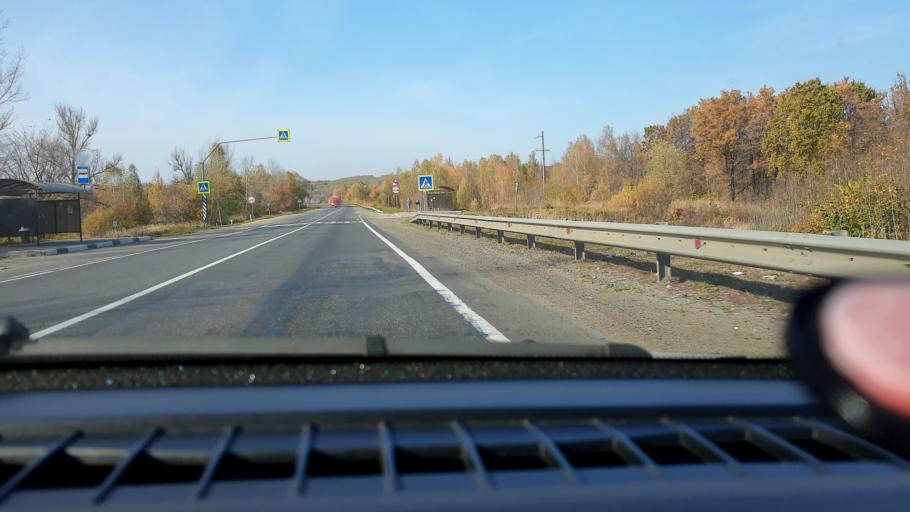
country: RU
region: Nizjnij Novgorod
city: Kstovo
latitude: 56.0929
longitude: 44.3242
